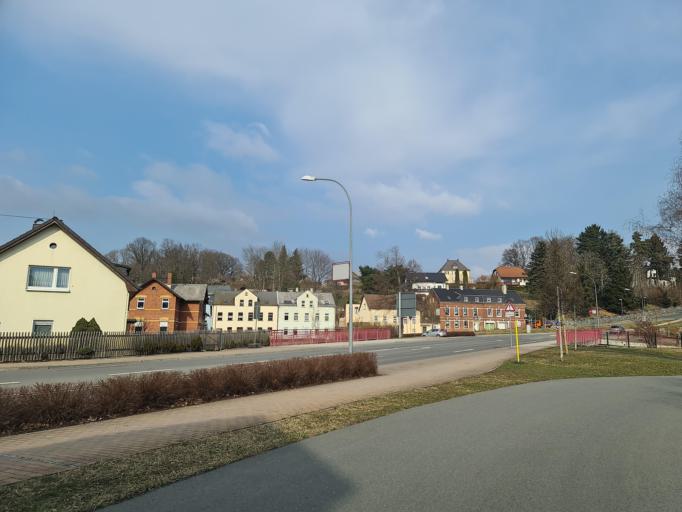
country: DE
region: Saxony
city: Rodewisch
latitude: 50.5325
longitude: 12.4044
